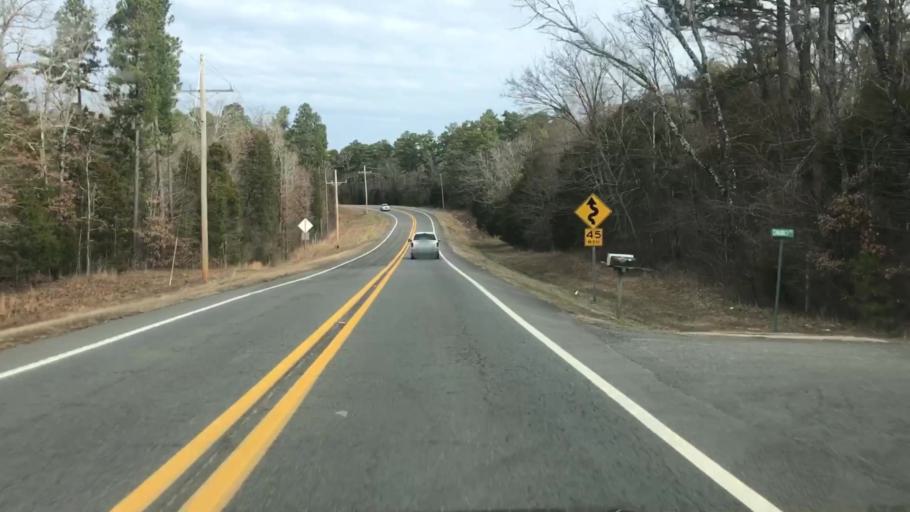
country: US
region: Arkansas
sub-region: Montgomery County
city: Mount Ida
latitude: 34.5860
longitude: -93.6634
